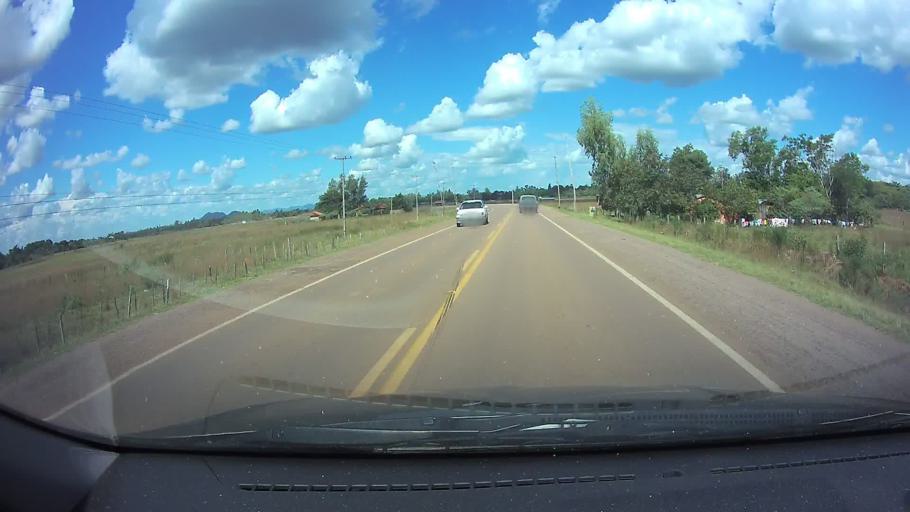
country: PY
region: Guaira
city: Itape
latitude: -25.9167
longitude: -56.6888
